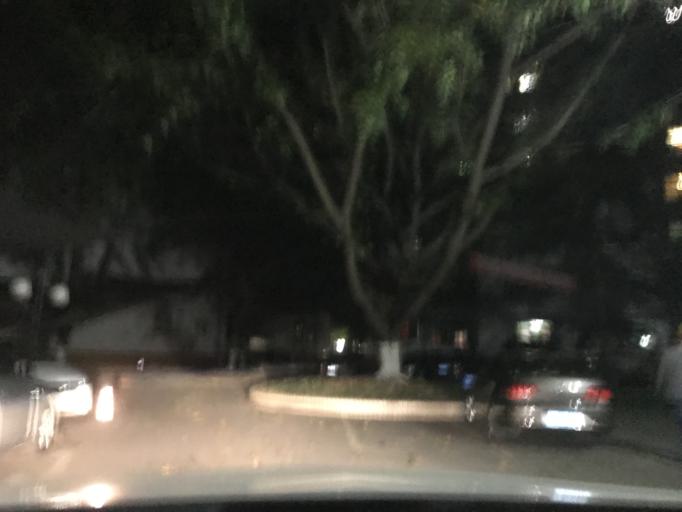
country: CN
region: Sichuan
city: Mianyang
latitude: 31.4538
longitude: 104.7606
